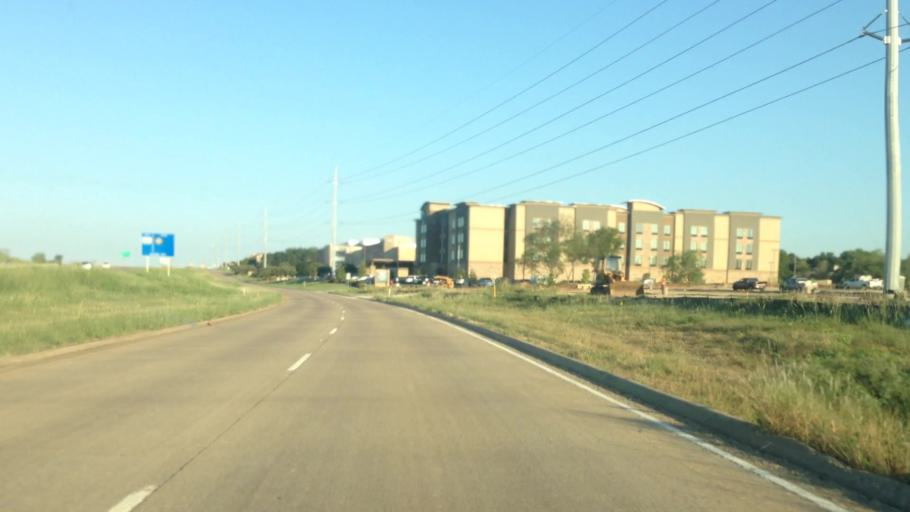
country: US
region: Texas
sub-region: Denton County
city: Trophy Club
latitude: 32.9869
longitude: -97.1718
